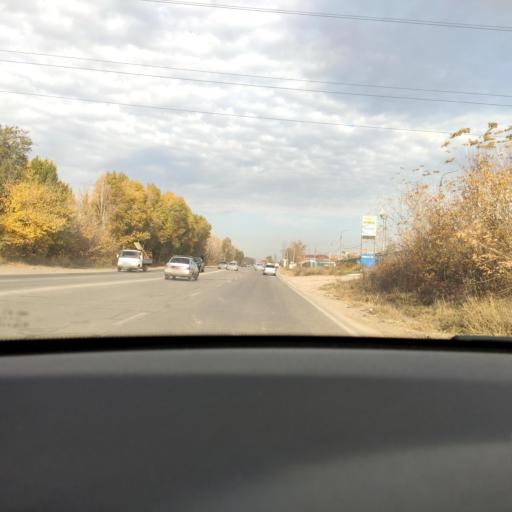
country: RU
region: Samara
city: Petra-Dubrava
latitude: 53.2611
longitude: 50.2900
